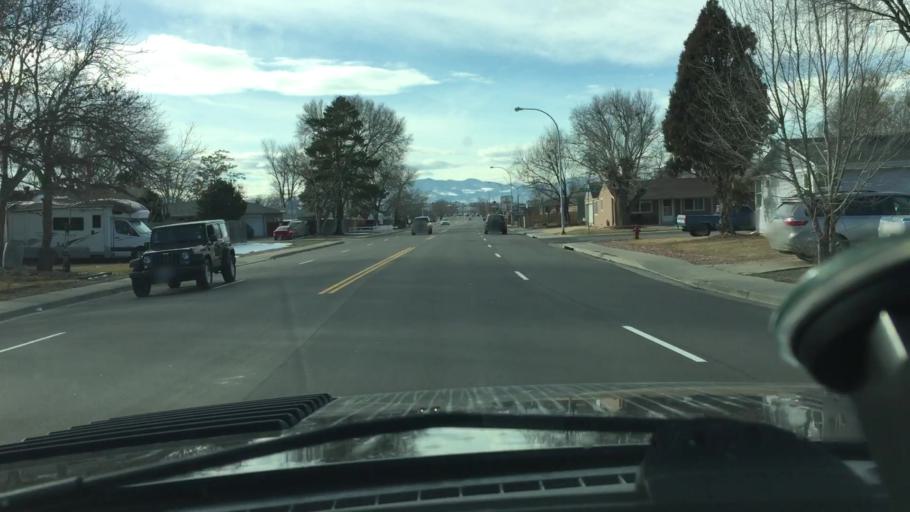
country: US
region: Colorado
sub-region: Adams County
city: Twin Lakes
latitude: 39.8273
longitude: -105.0178
